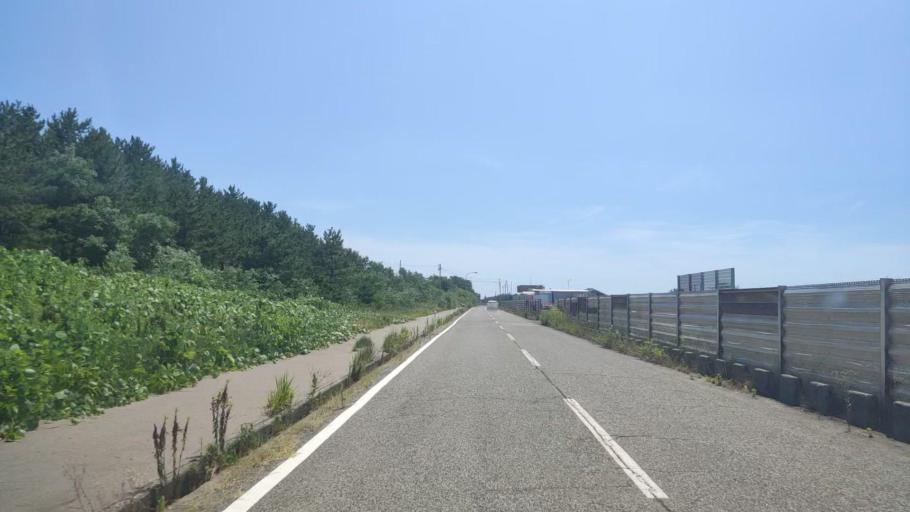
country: JP
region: Ishikawa
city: Kanazawa-shi
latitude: 36.6093
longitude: 136.5953
